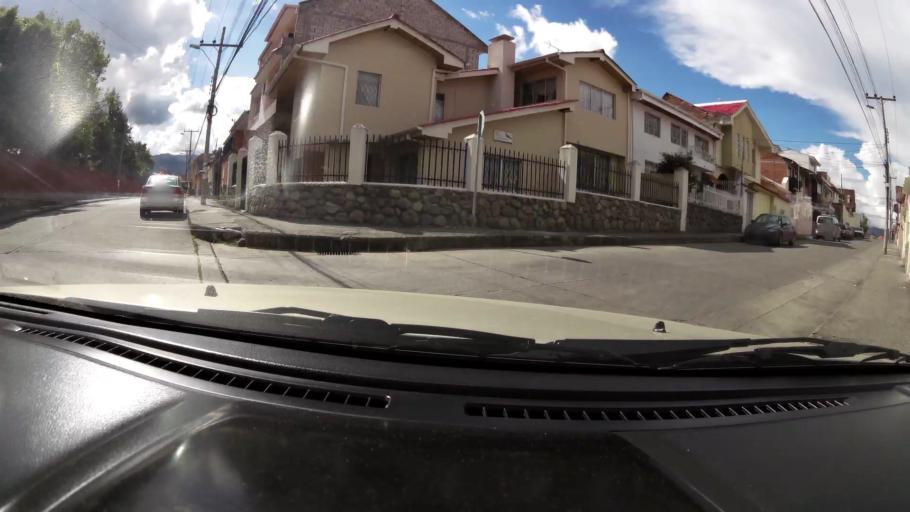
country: EC
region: Azuay
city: Cuenca
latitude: -2.8874
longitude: -78.9981
